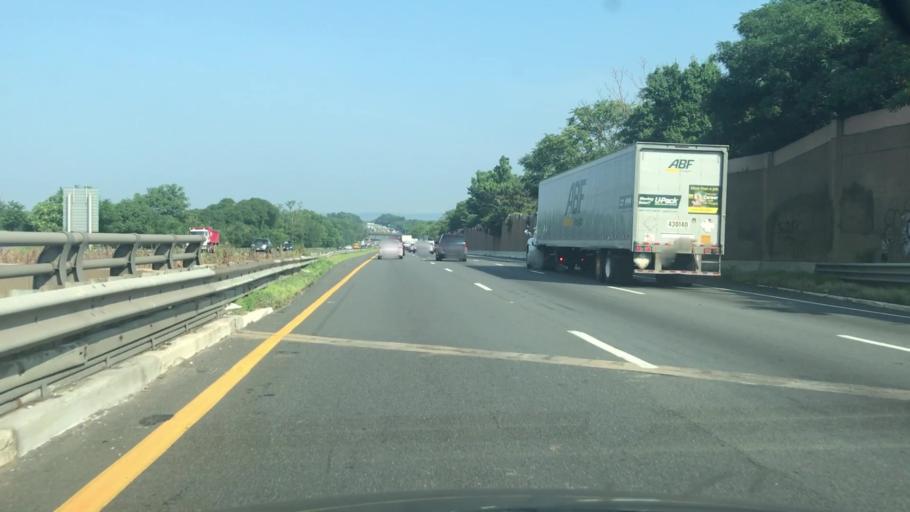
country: US
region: New Jersey
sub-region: Middlesex County
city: Metuchen
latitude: 40.5361
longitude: -74.3807
